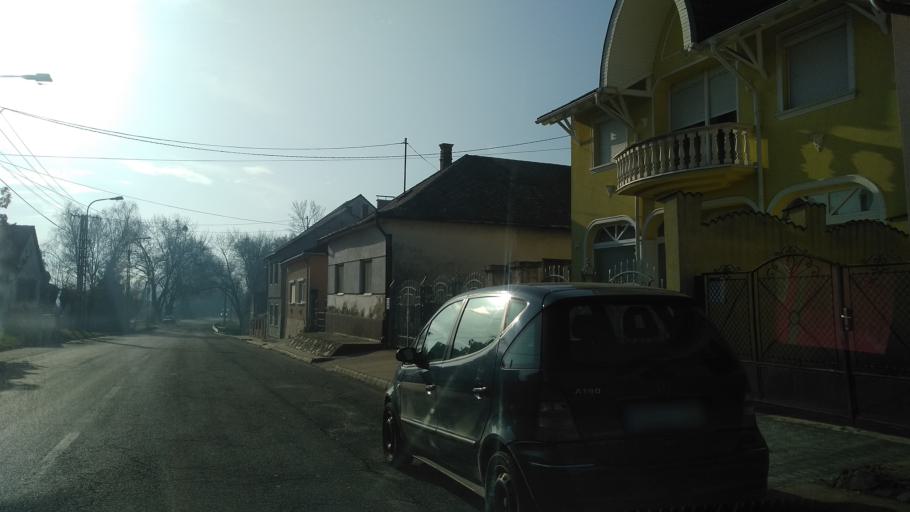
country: HU
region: Somogy
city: Barcs
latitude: 45.9575
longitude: 17.4634
